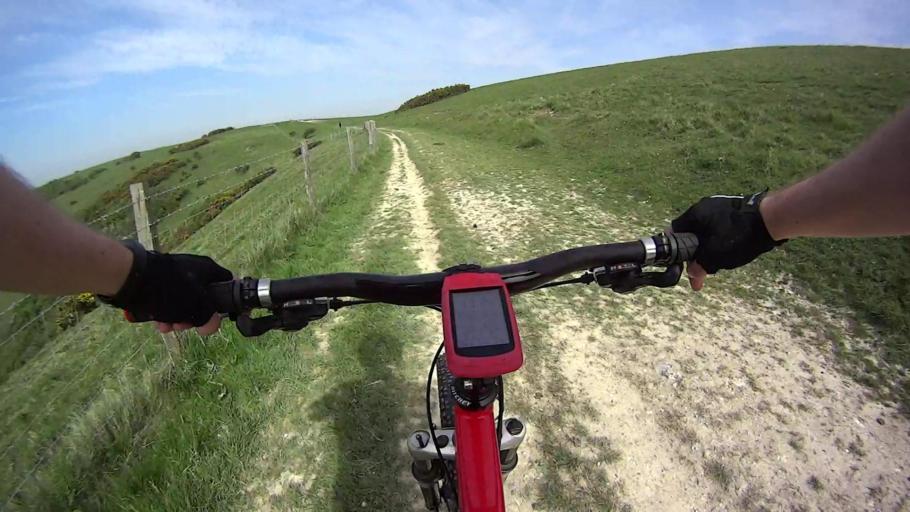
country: GB
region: England
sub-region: East Sussex
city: Hailsham
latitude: 50.8081
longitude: 0.1930
